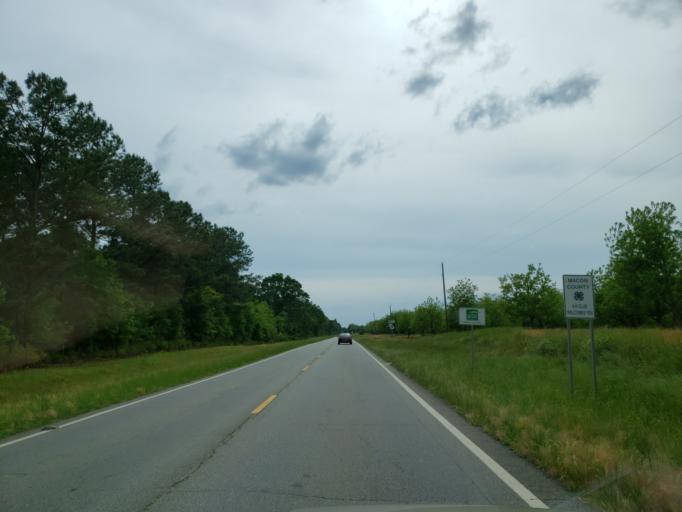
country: US
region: Georgia
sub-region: Macon County
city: Marshallville
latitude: 32.4229
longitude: -83.8370
